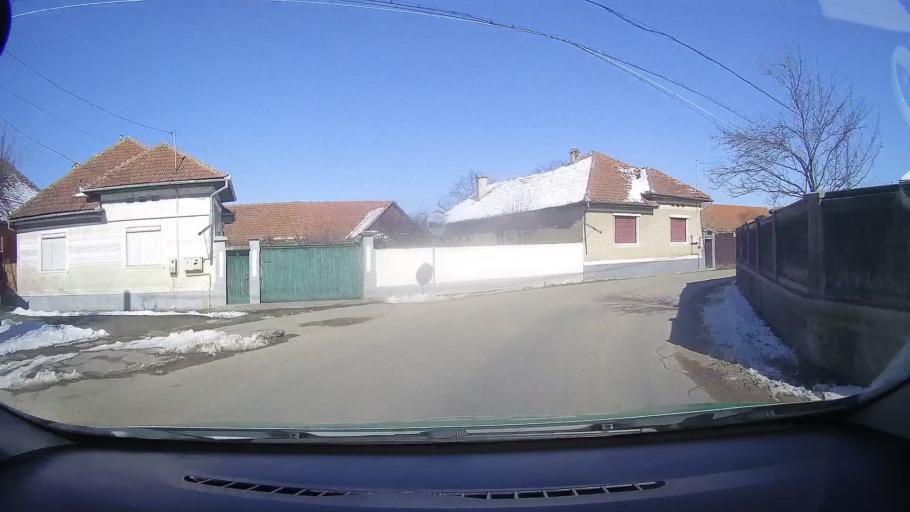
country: RO
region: Brasov
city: Ucea de Sus
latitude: 45.7509
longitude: 24.6790
